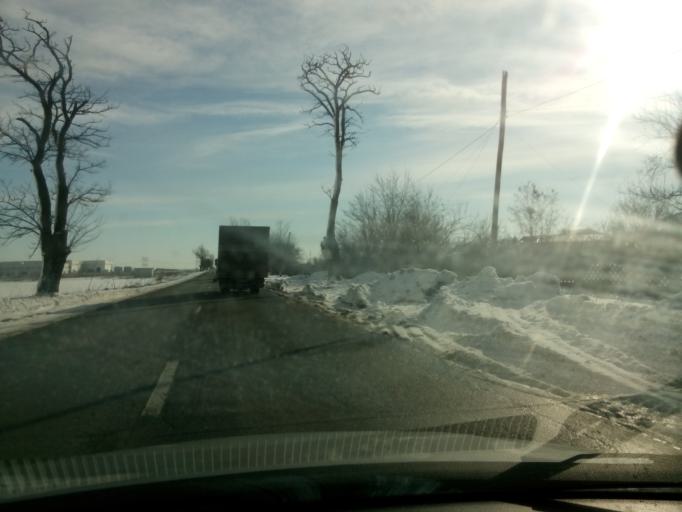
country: RO
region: Ilfov
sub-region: Comuna Berceni
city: Berceni
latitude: 44.3556
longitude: 26.2077
